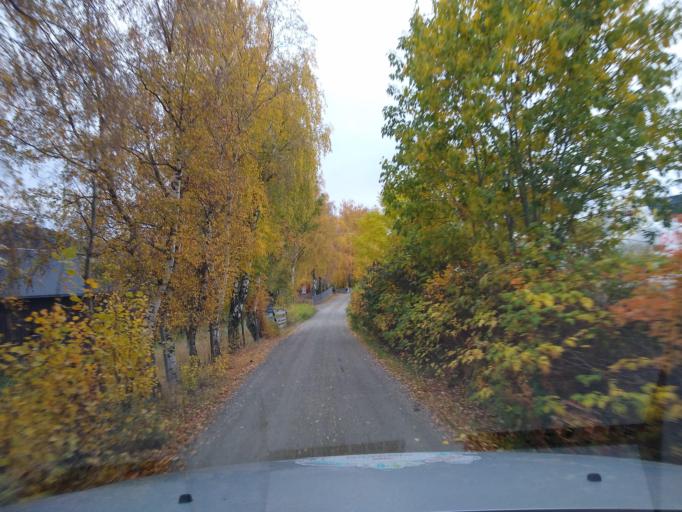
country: NO
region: Oppland
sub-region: Ringebu
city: Ringebu
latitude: 61.5428
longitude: 10.1278
